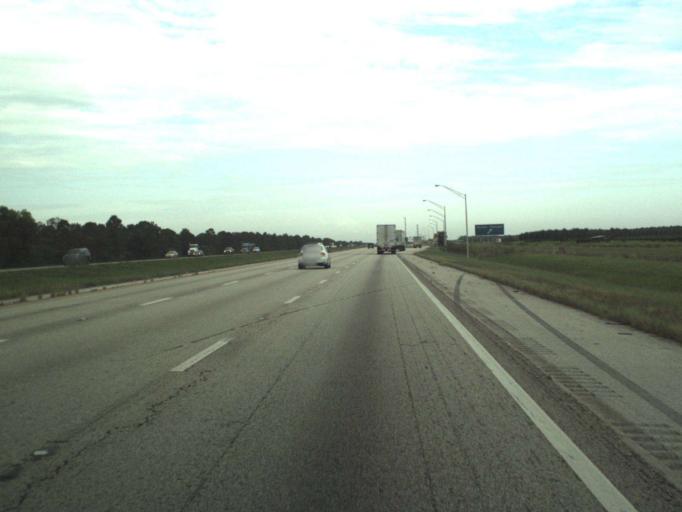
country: US
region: Florida
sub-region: Palm Beach County
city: Tequesta
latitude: 26.9955
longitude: -80.1955
